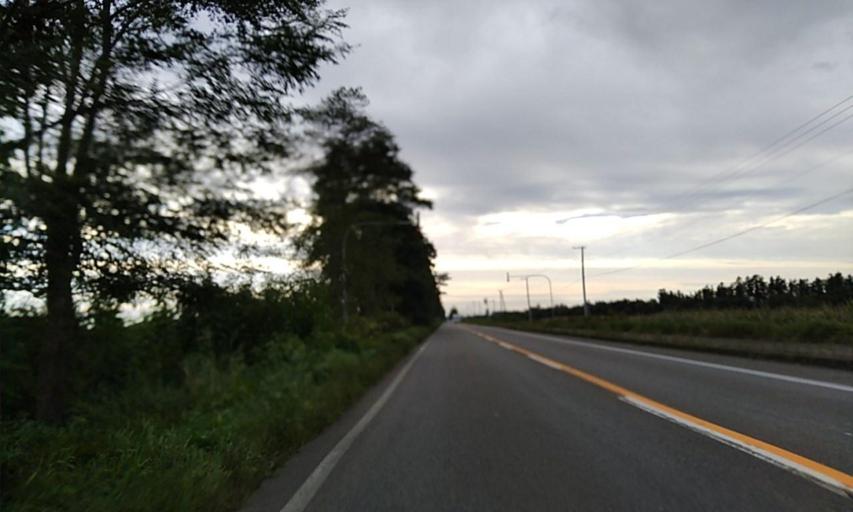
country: JP
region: Hokkaido
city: Obihiro
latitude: 42.9307
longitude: 142.9783
